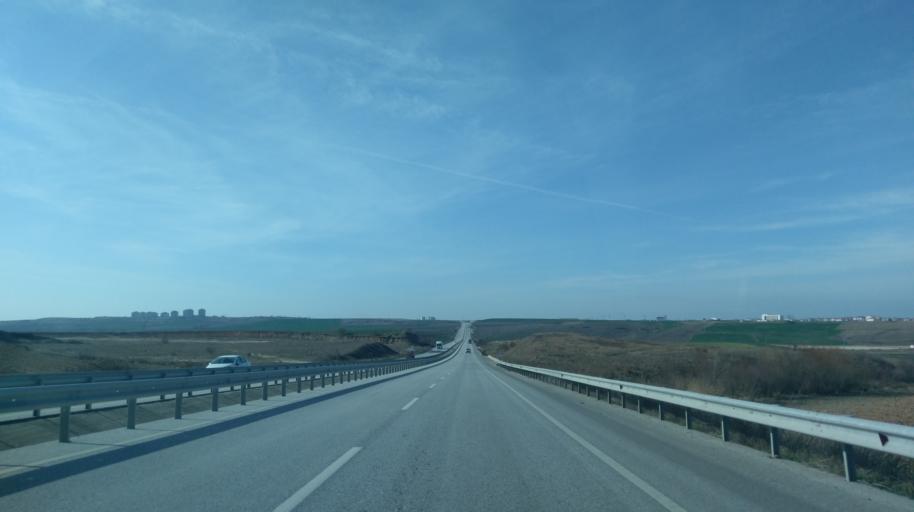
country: TR
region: Edirne
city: Uzun Keupru
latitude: 41.2558
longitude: 26.7070
